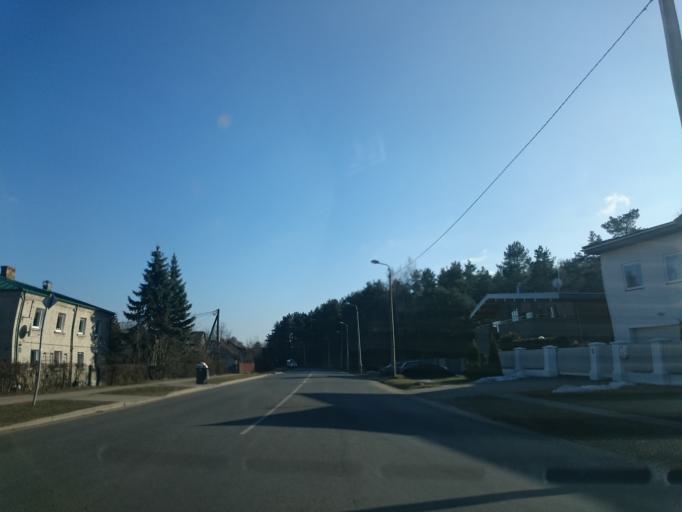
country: LV
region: Riga
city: Bergi
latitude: 56.9826
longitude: 24.2407
